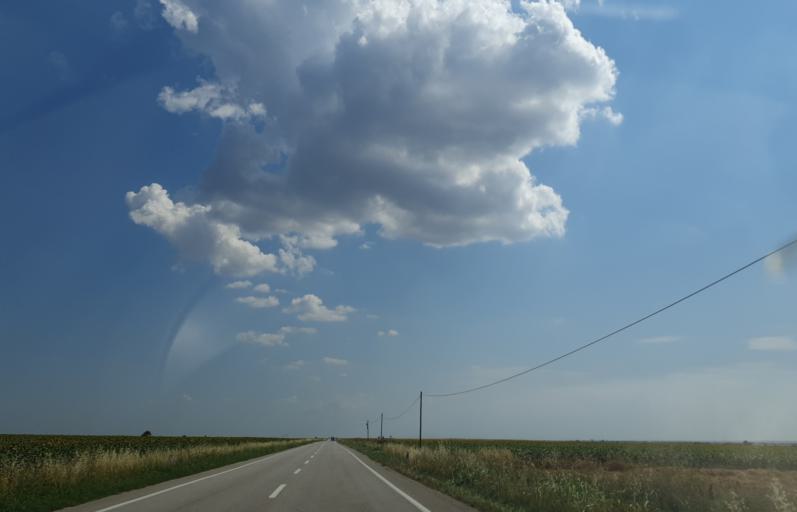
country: TR
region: Kirklareli
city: Buyukkaristiran
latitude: 41.4196
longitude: 27.5793
